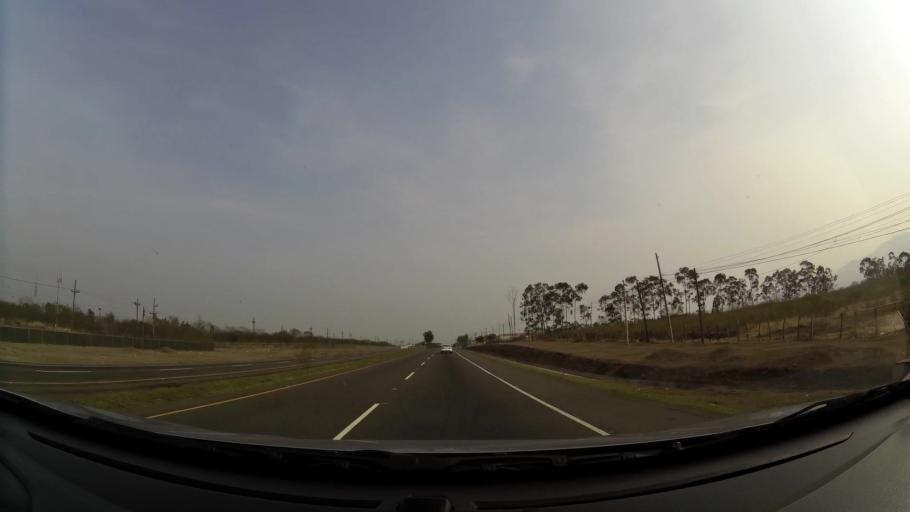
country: HN
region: La Paz
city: Yarumela
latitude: 14.3895
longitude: -87.6134
